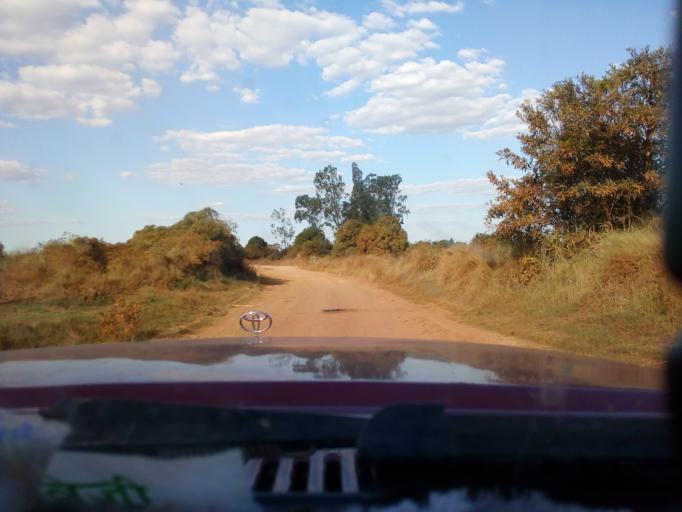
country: MG
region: Boeny
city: Mahajanga
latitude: -15.9611
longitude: 45.9639
